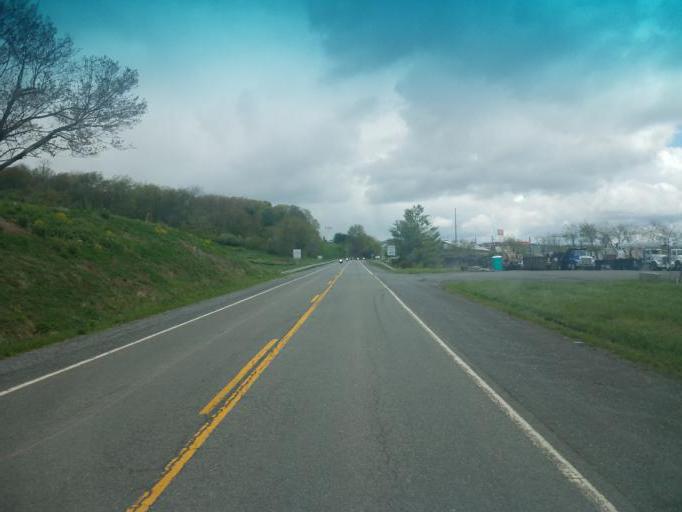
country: US
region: Virginia
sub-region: Bland County
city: Bland
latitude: 37.0979
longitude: -81.1335
